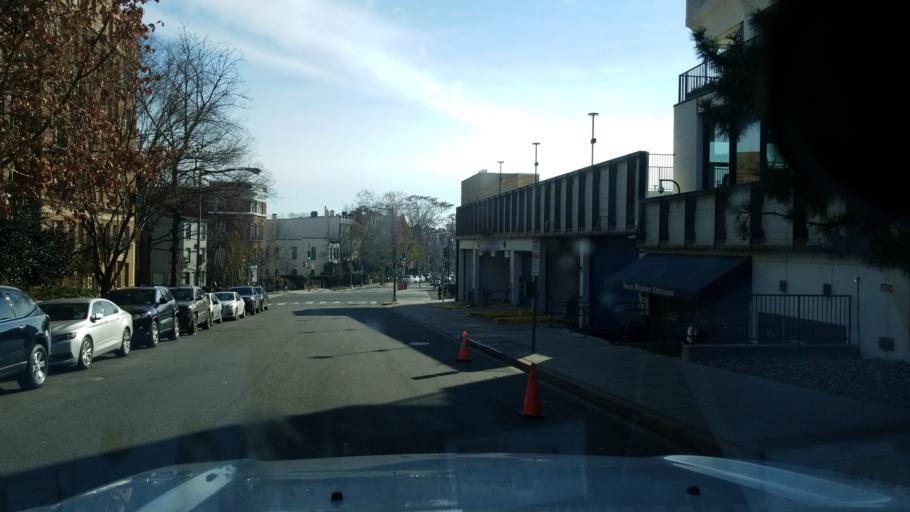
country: US
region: Washington, D.C.
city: Washington, D.C.
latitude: 38.9166
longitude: -77.0437
